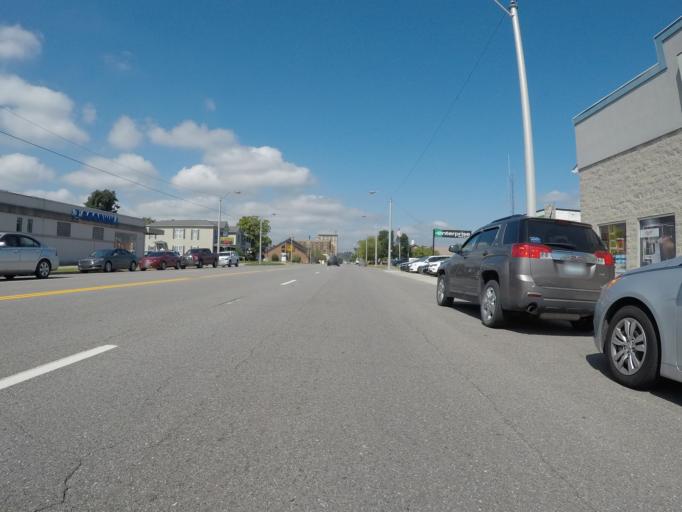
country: US
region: Kentucky
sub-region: Boyd County
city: Ashland
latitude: 38.4756
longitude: -82.6333
